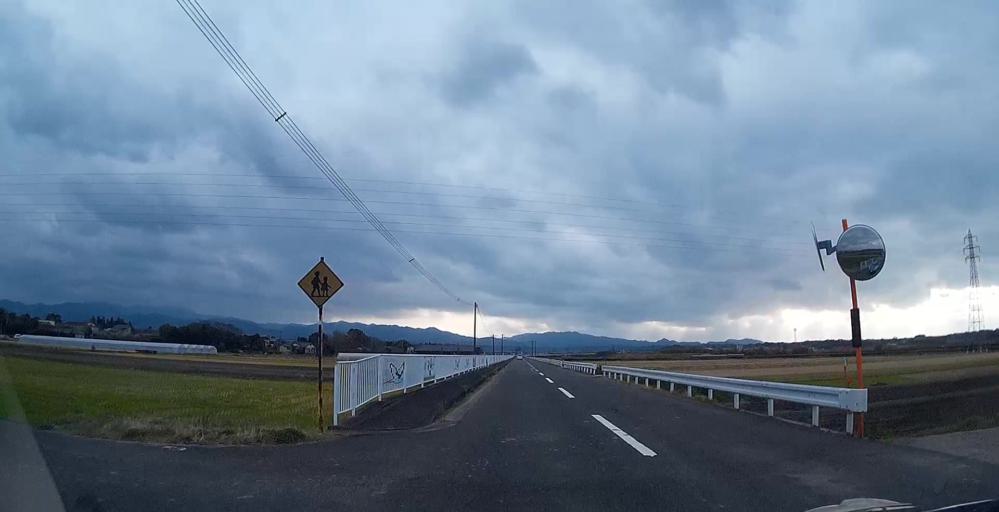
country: JP
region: Kagoshima
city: Izumi
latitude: 32.0892
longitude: 130.2763
